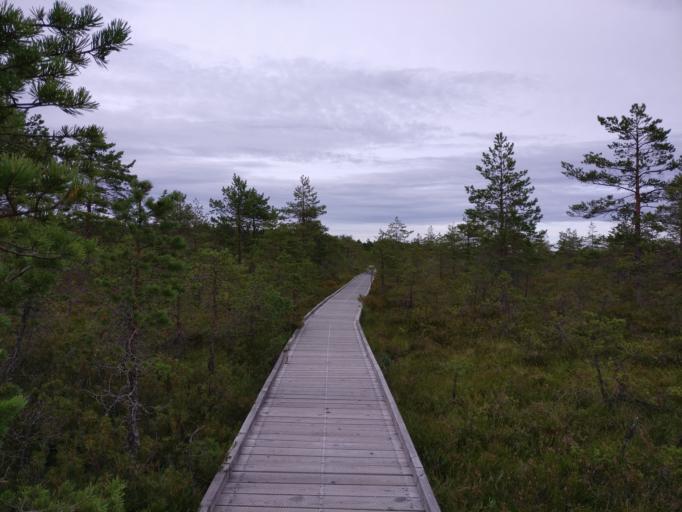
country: EE
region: Paernumaa
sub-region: Vaendra vald (alev)
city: Vandra
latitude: 58.4899
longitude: 24.9823
